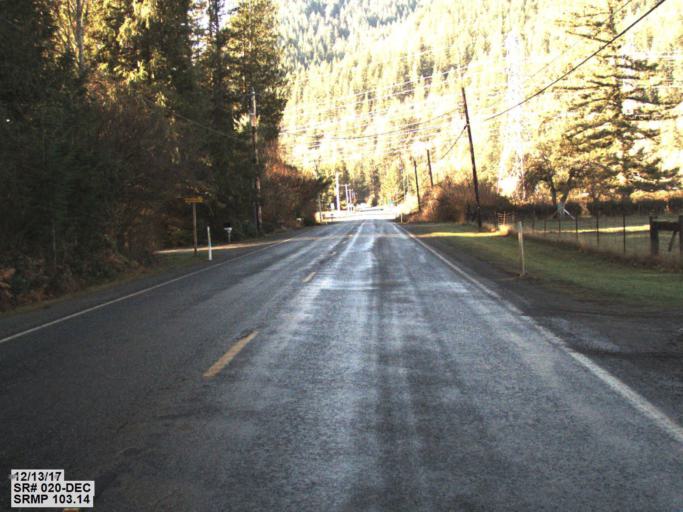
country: US
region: Washington
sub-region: Snohomish County
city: Darrington
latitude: 48.5088
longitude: -121.4803
